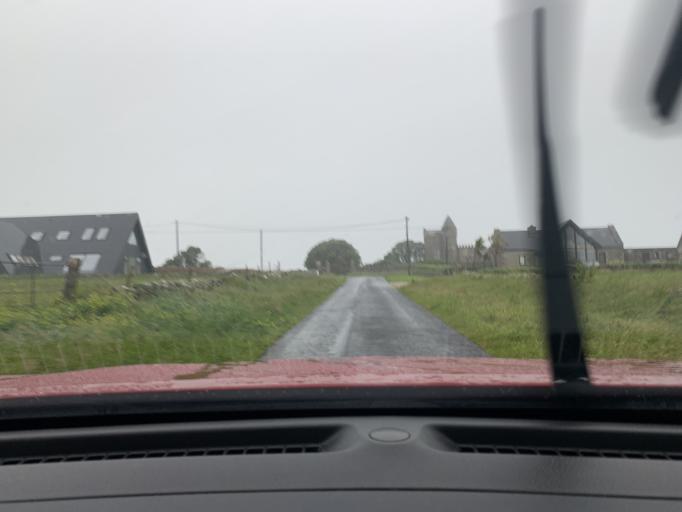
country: IE
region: Ulster
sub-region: County Donegal
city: Killybegs
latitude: 54.4689
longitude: -8.4547
